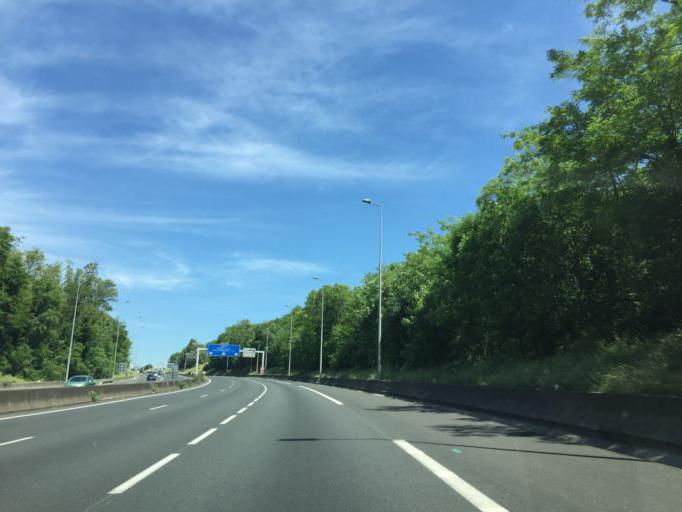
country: FR
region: Rhone-Alpes
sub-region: Departement du Rhone
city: Rillieux-la-Pape
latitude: 45.8171
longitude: 4.9183
